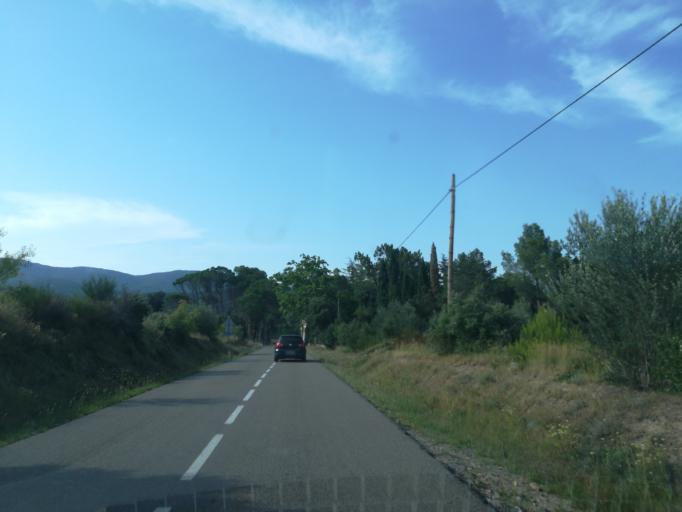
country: ES
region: Catalonia
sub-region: Provincia de Girona
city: Agullana
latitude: 42.3911
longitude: 2.8518
